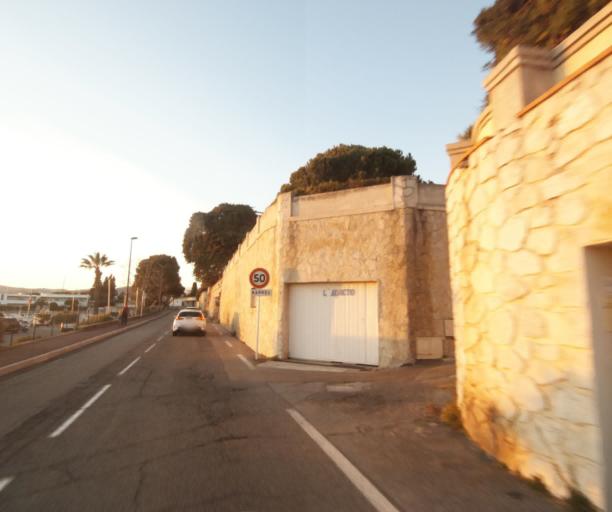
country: FR
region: Provence-Alpes-Cote d'Azur
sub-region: Departement des Alpes-Maritimes
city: Antibes
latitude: 43.5606
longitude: 7.1204
